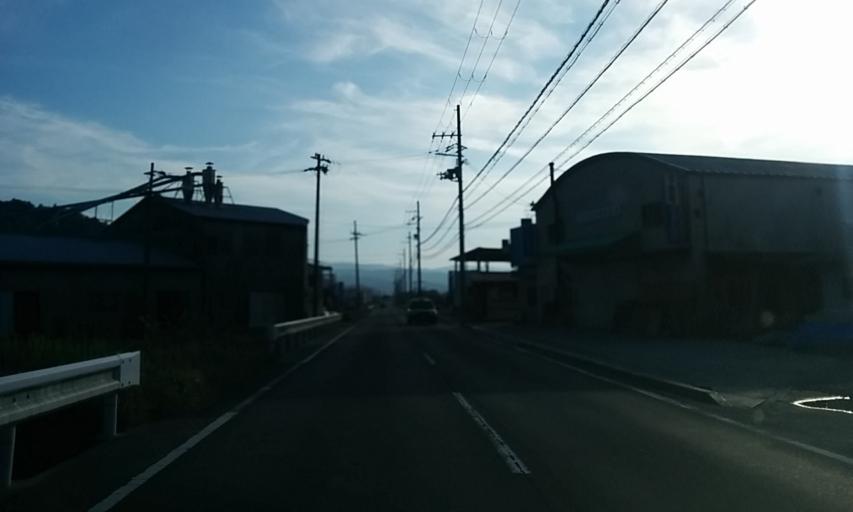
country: JP
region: Kyoto
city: Kameoka
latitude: 35.1316
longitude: 135.4857
